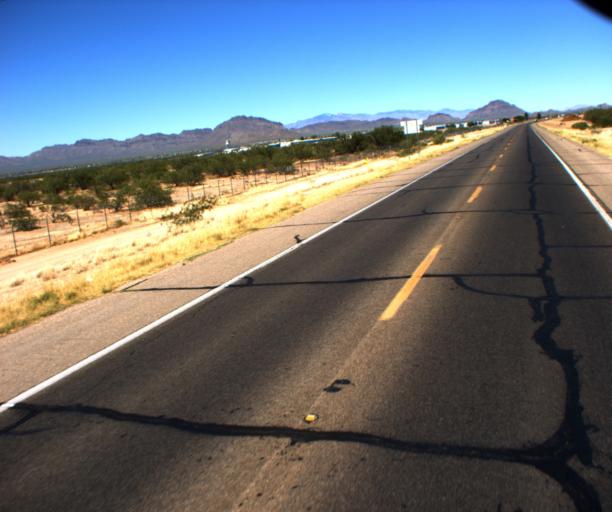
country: US
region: Arizona
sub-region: Pima County
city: Valencia West
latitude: 32.1303
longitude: -111.1825
